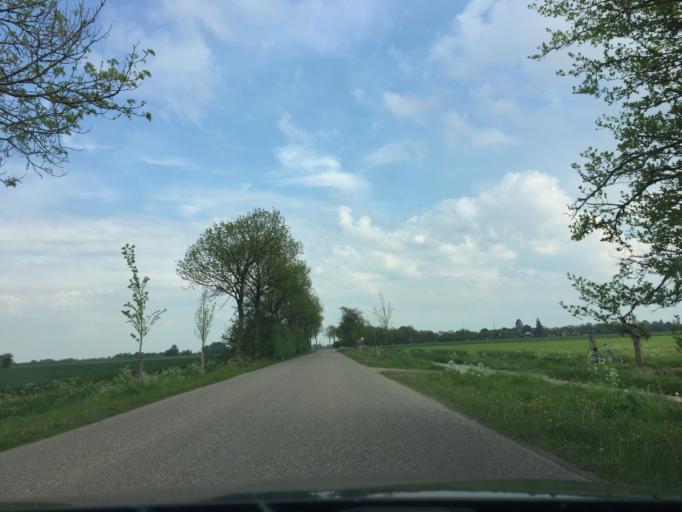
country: NL
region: Groningen
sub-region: Gemeente Zuidhorn
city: Oldehove
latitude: 53.3073
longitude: 6.3790
